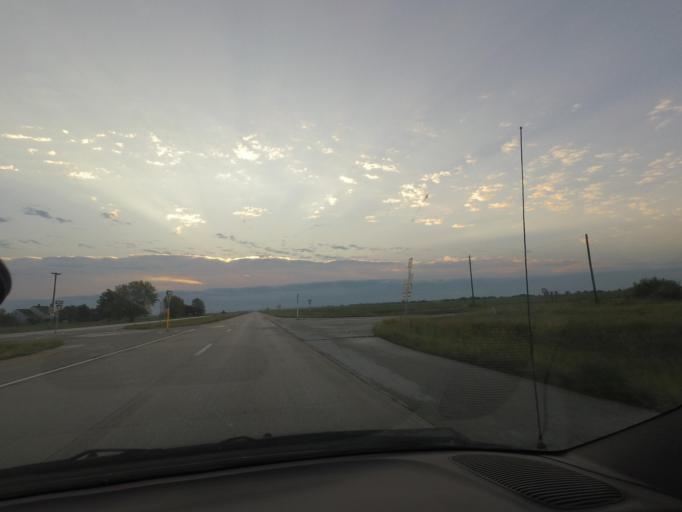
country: US
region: Missouri
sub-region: Macon County
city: Macon
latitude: 39.7501
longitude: -92.3323
